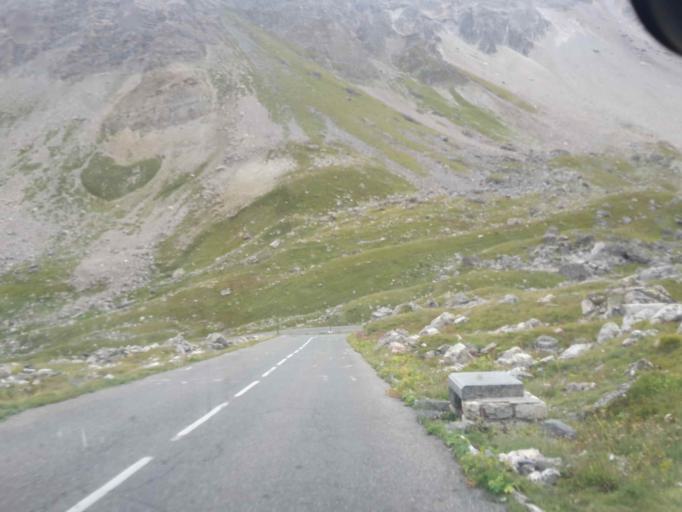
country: FR
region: Rhone-Alpes
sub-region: Departement de la Savoie
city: Valloire
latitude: 45.0787
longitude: 6.4237
